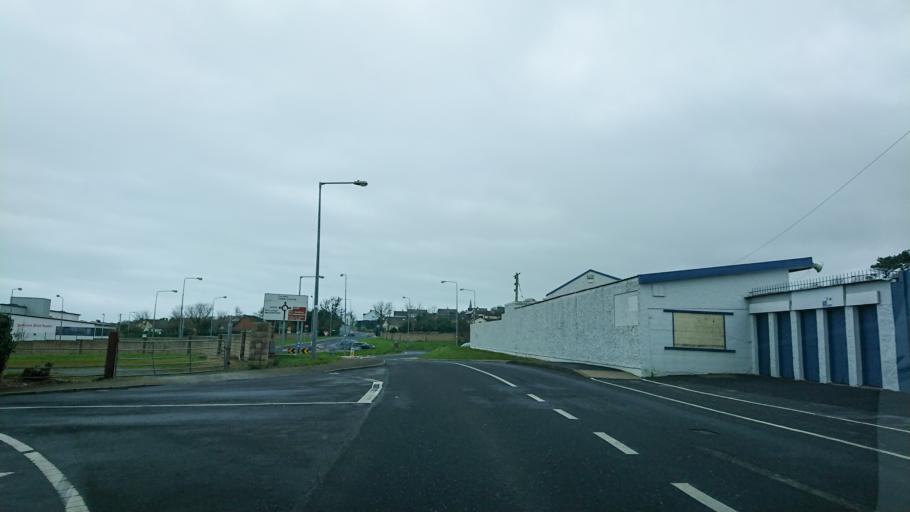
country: IE
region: Munster
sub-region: Waterford
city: Tra Mhor
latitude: 52.1704
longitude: -7.1466
